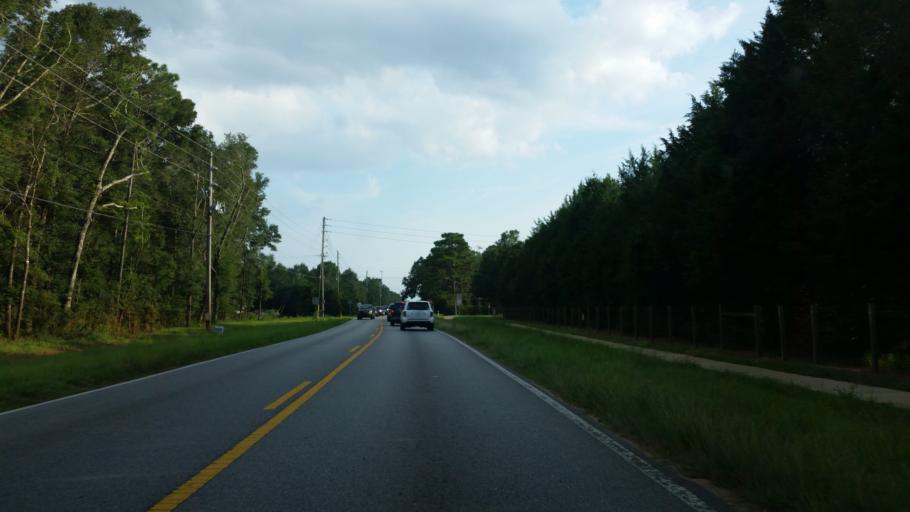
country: US
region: Florida
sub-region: Santa Rosa County
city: Pace
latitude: 30.6190
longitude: -87.1317
